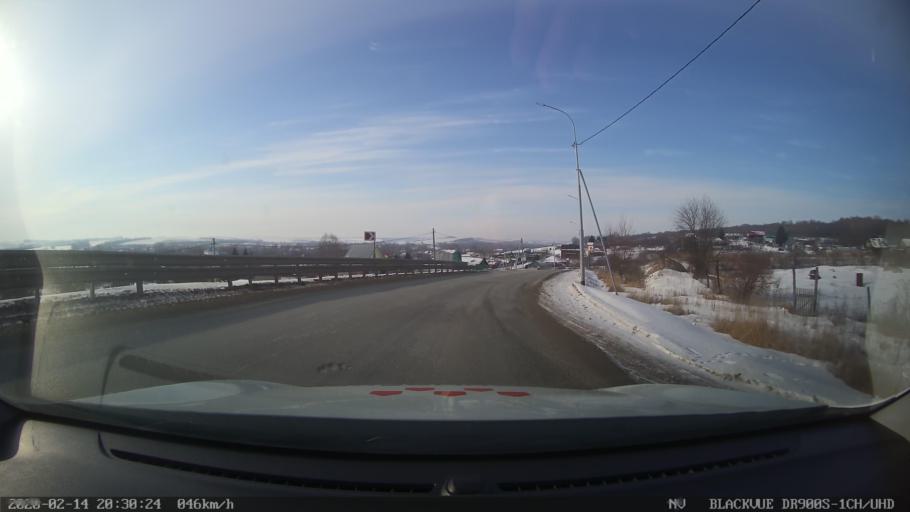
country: RU
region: Tatarstan
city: Stolbishchi
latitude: 55.4431
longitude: 48.9942
